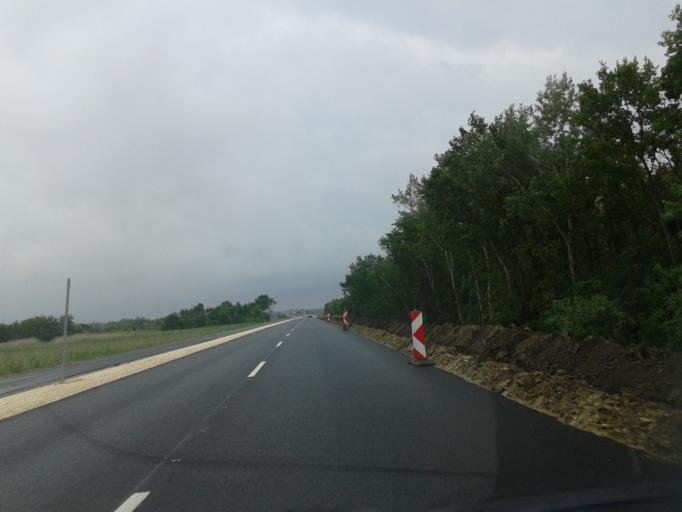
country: HU
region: Csongrad
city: Domaszek
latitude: 46.2521
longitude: 20.0703
